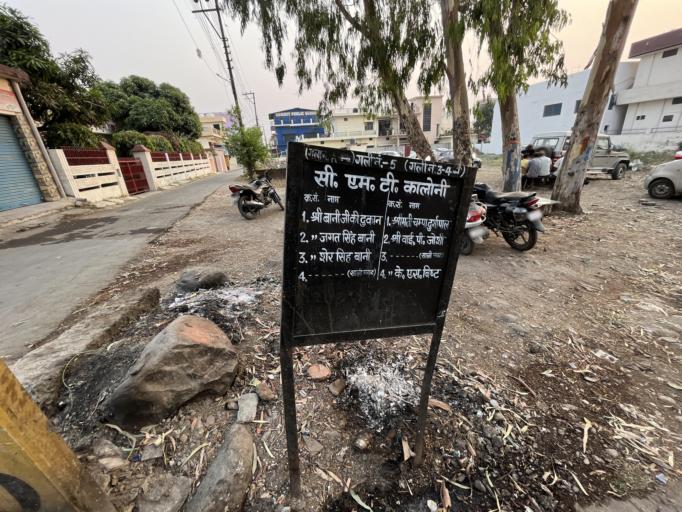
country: IN
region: Uttarakhand
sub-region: Naini Tal
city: Haldwani
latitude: 29.2001
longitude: 79.5114
